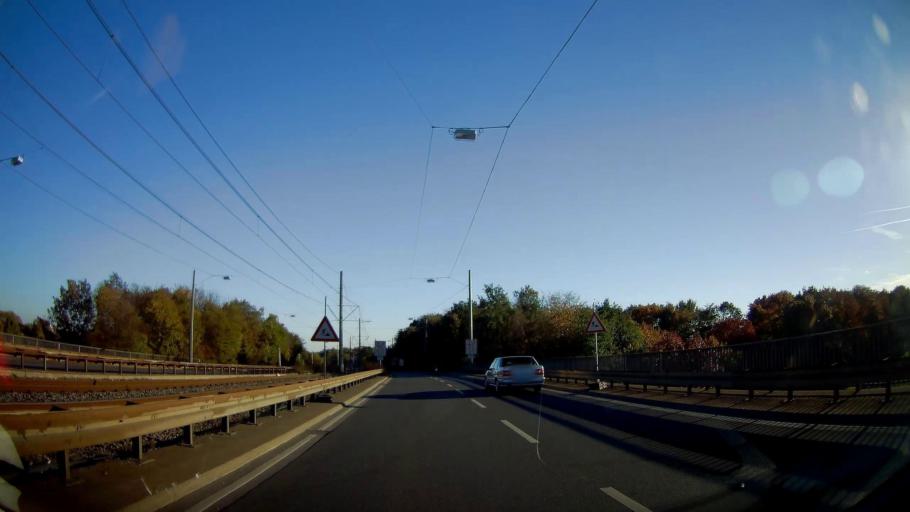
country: DE
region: North Rhine-Westphalia
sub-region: Regierungsbezirk Munster
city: Gelsenkirchen
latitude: 51.5394
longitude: 7.0696
